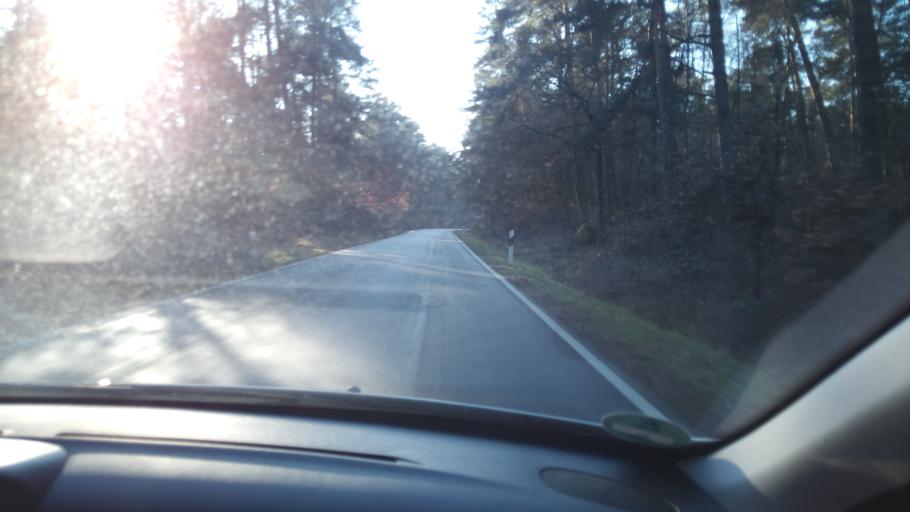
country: DE
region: Schleswig-Holstein
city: Gottin
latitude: 53.5134
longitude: 10.6957
